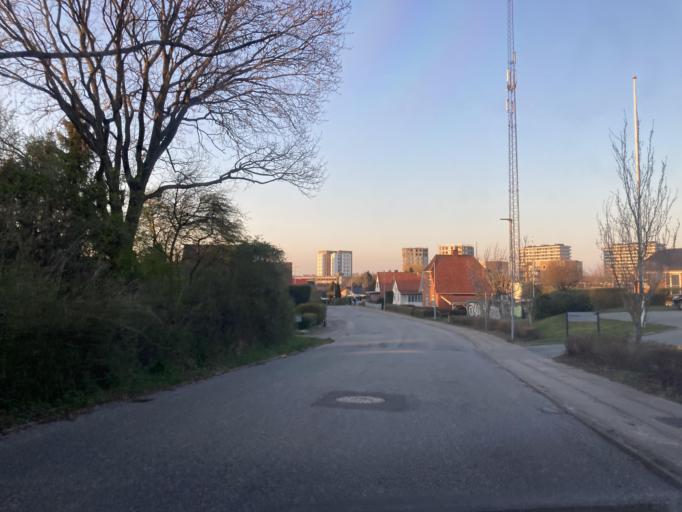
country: DK
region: South Denmark
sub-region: Kolding Kommune
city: Kolding
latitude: 55.4826
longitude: 9.4952
